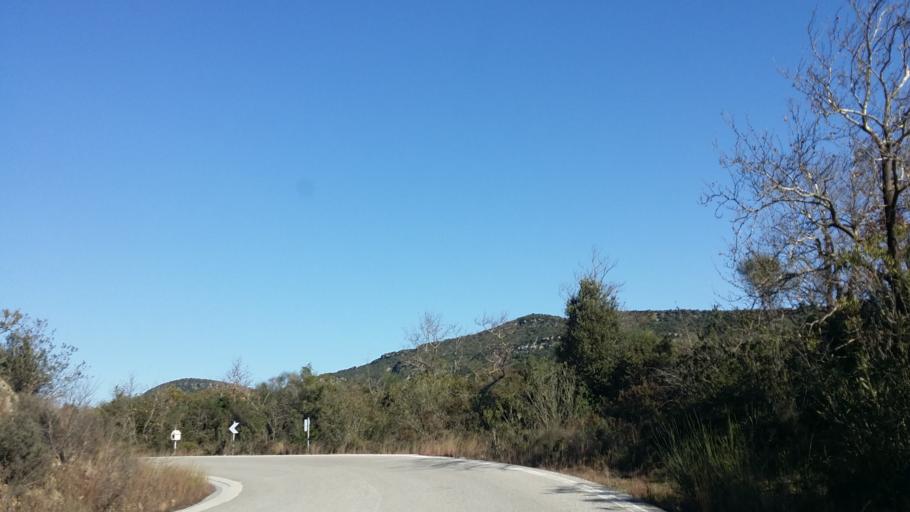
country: GR
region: West Greece
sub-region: Nomos Aitolias kai Akarnanias
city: Lepenou
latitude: 38.7677
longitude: 21.3368
